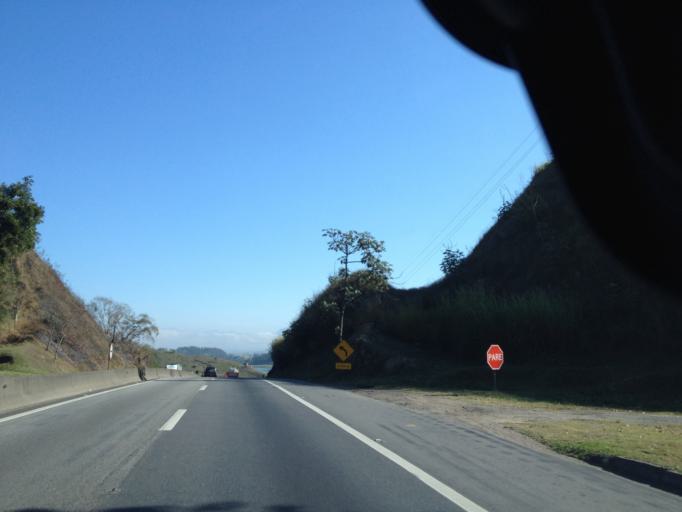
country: BR
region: Rio de Janeiro
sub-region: Porto Real
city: Porto Real
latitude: -22.4771
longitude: -44.2638
